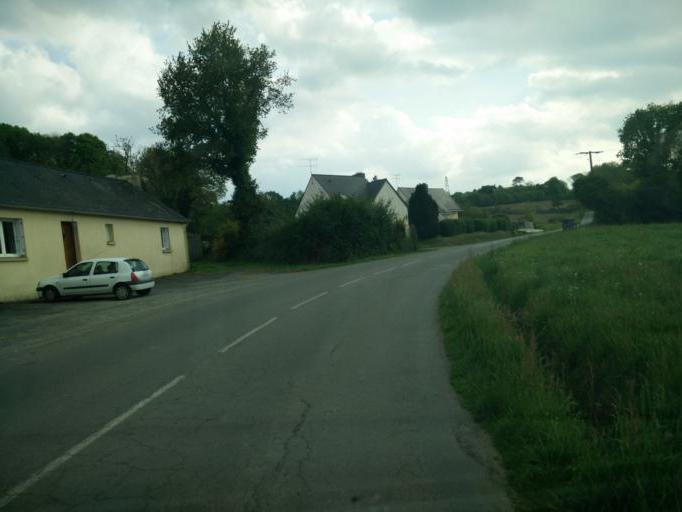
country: FR
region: Brittany
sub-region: Departement du Finistere
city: Tremeven
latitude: 47.9118
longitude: -3.5117
